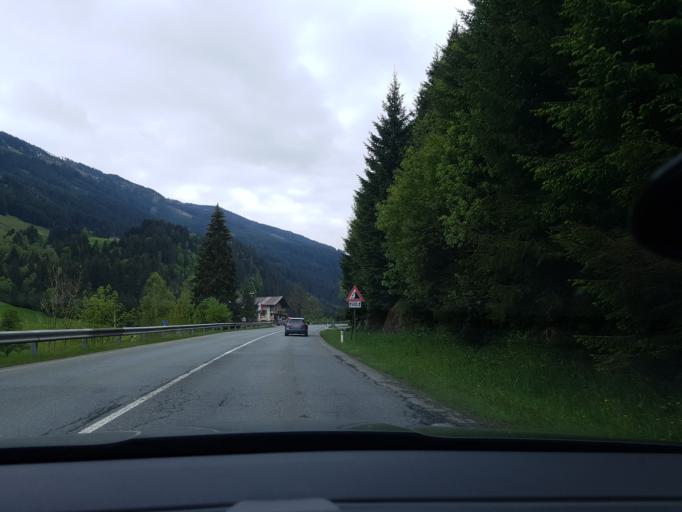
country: AT
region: Tyrol
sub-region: Politischer Bezirk Kitzbuhel
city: Jochberg
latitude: 47.3557
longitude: 12.4140
